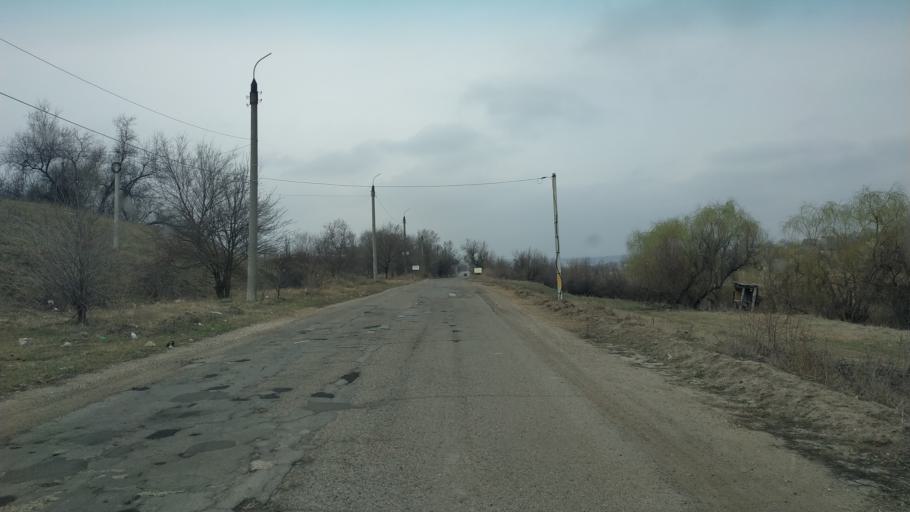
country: MD
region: Chisinau
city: Singera
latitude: 46.9119
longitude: 29.0135
